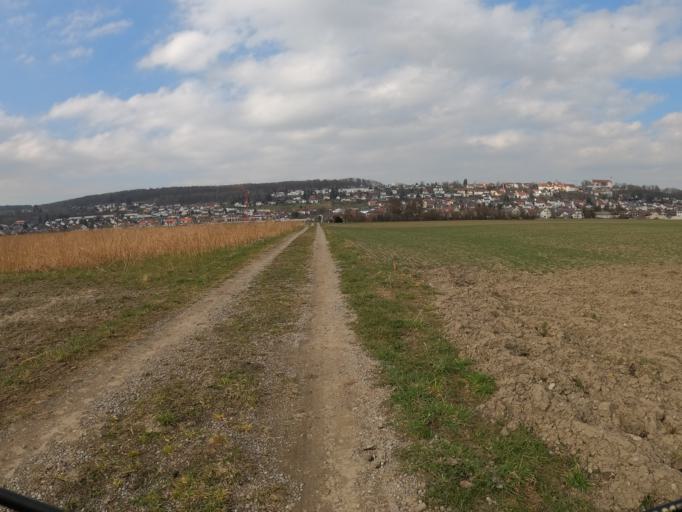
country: DE
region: Bavaria
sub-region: Swabia
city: Nersingen
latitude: 48.4426
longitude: 10.0832
